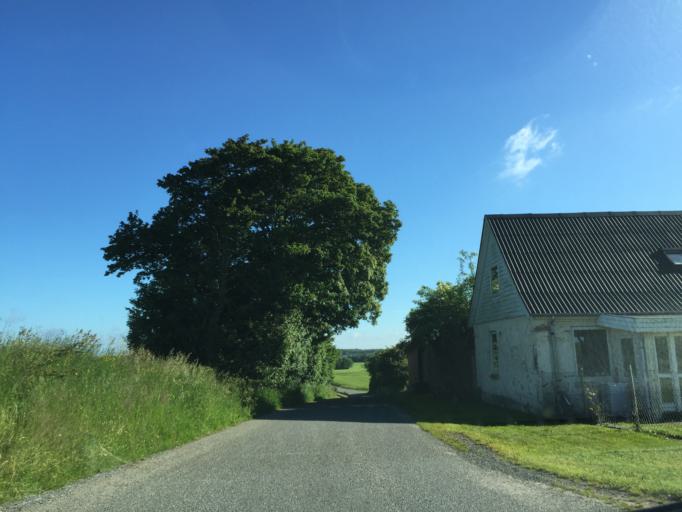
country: DK
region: Central Jutland
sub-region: Viborg Kommune
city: Bjerringbro
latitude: 56.2610
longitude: 9.6896
